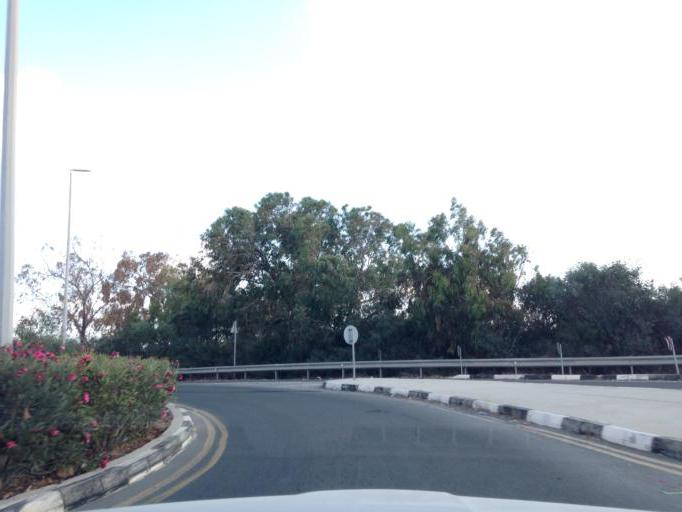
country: CY
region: Pafos
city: Paphos
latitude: 34.7099
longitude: 32.4902
